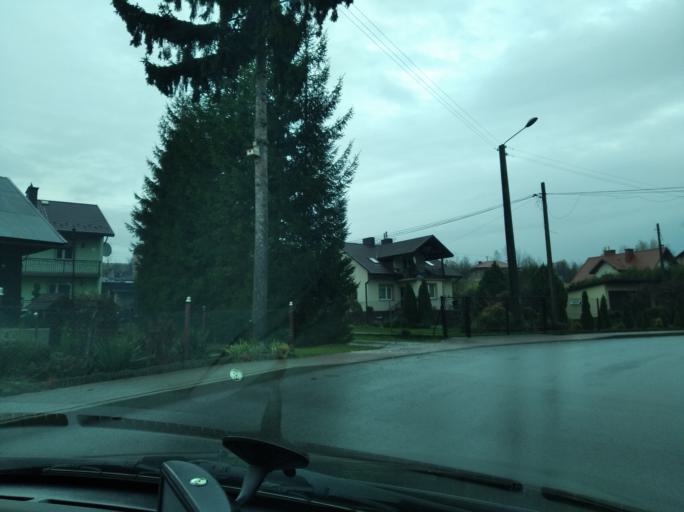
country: PL
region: Subcarpathian Voivodeship
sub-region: Powiat rzeszowski
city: Lubenia
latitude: 49.9254
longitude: 21.9438
